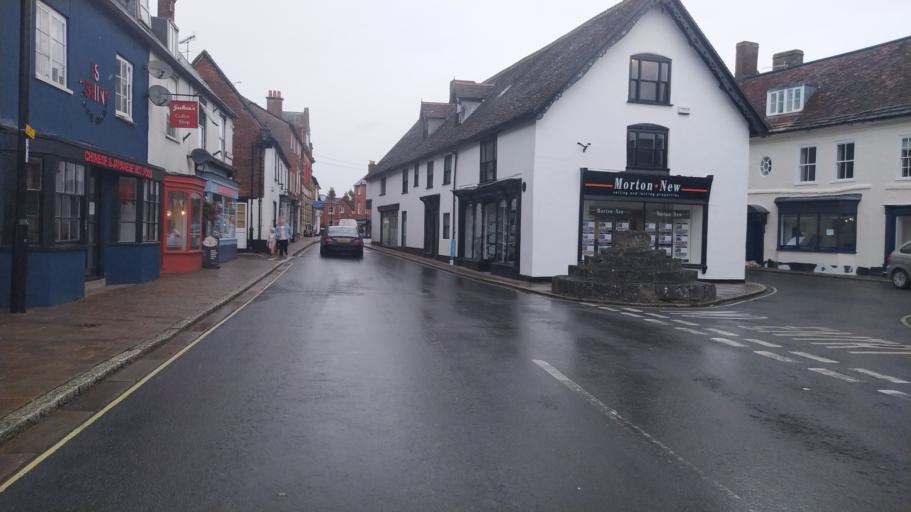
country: GB
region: England
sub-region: Dorset
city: Sturminster Newton
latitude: 50.9257
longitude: -2.3053
